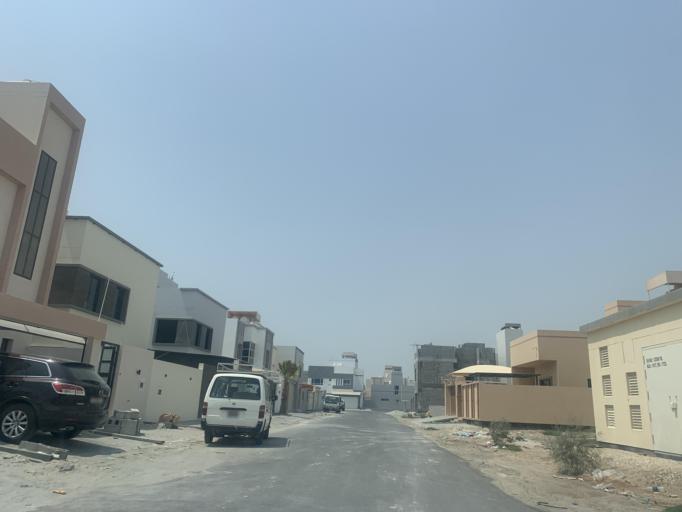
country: BH
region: Central Governorate
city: Madinat Hamad
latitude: 26.1279
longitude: 50.4688
